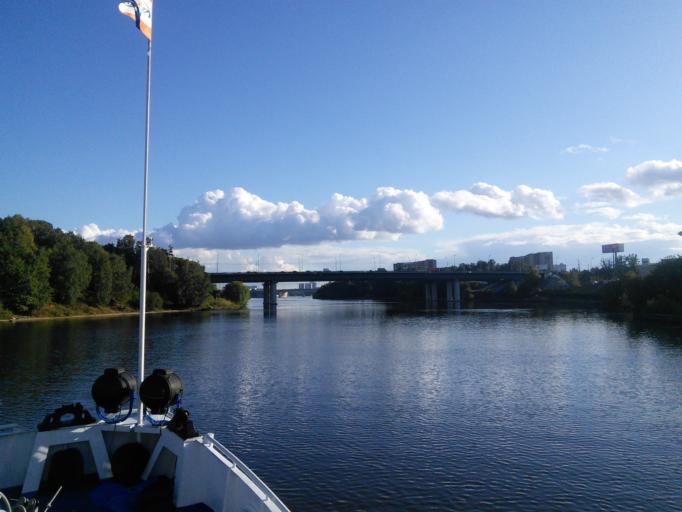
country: RU
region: Moskovskaya
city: Levoberezhnaya
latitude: 55.8861
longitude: 37.4592
